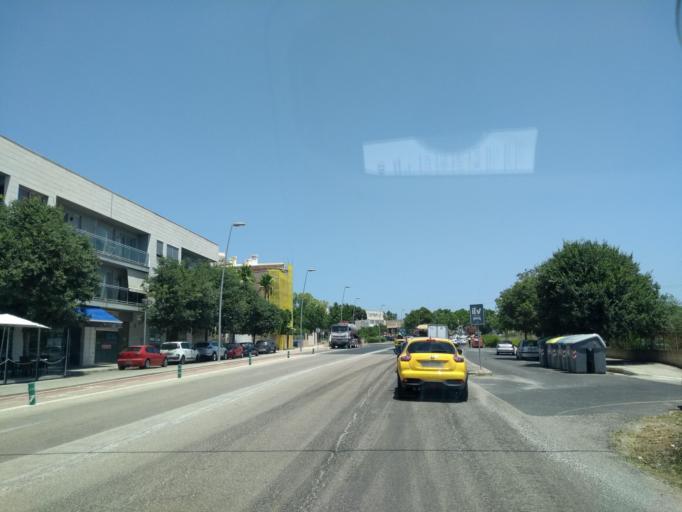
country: ES
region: Balearic Islands
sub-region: Illes Balears
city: Inca
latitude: 39.7246
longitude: 2.9202
